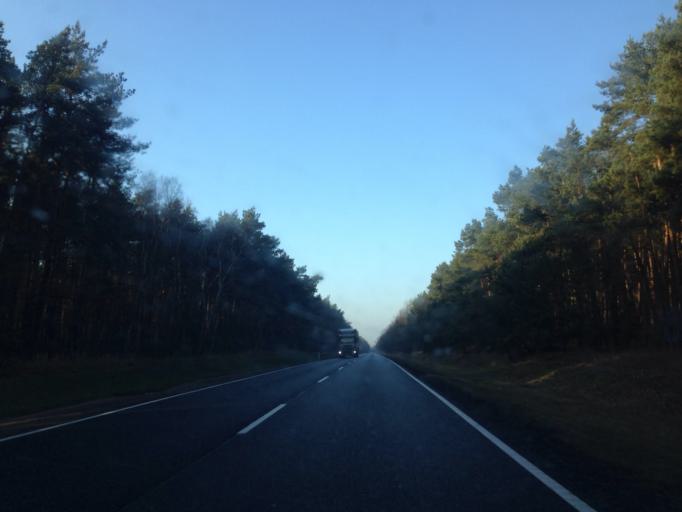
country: PL
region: Kujawsko-Pomorskie
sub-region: Powiat torunski
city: Zlawies Wielka
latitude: 53.0376
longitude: 18.3963
